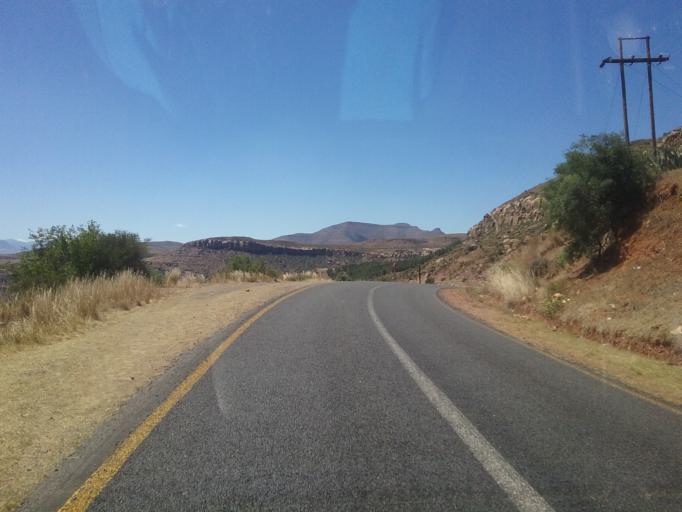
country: LS
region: Quthing
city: Quthing
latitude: -30.2798
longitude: 27.7478
